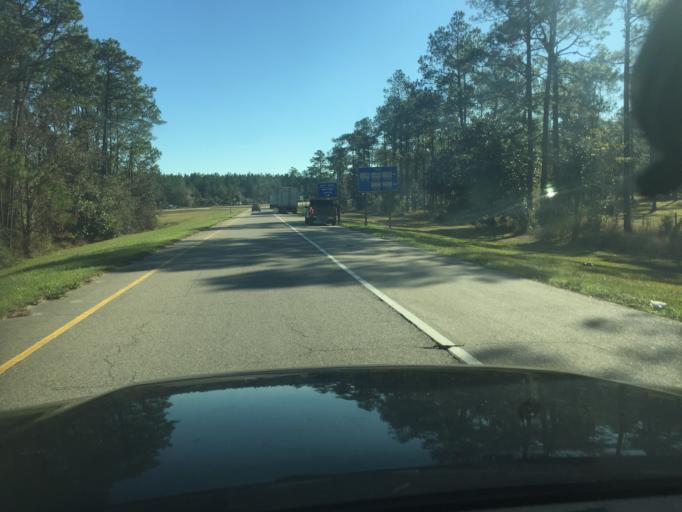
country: US
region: Mississippi
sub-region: Hancock County
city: Pearlington
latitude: 30.3146
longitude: -89.5989
